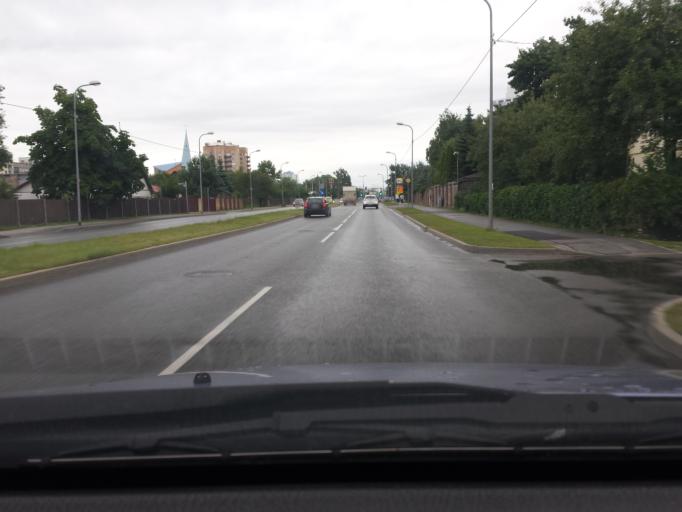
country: LV
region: Riga
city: Riga
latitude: 56.9473
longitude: 24.1842
